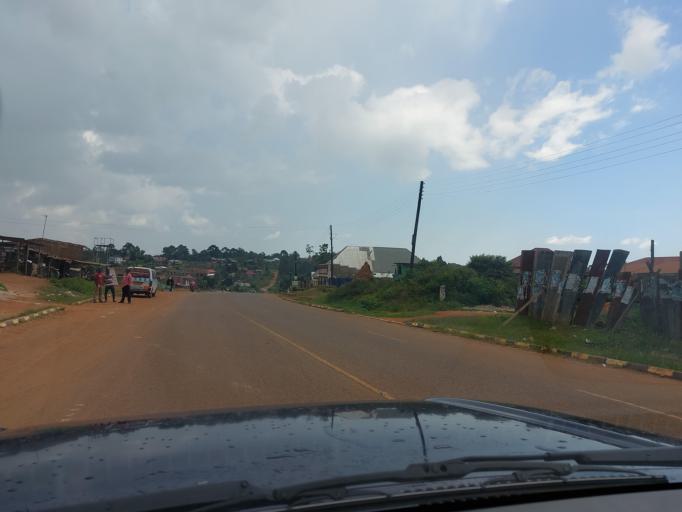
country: UG
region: Central Region
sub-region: Buikwe District
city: Buikwe
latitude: 0.2392
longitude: 32.9232
